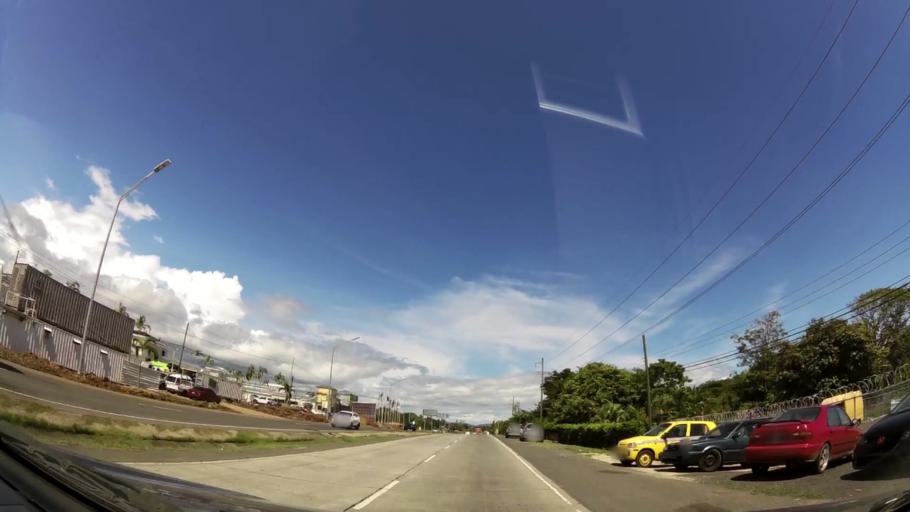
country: PA
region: Panama
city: Chame
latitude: 8.5517
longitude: -79.9083
